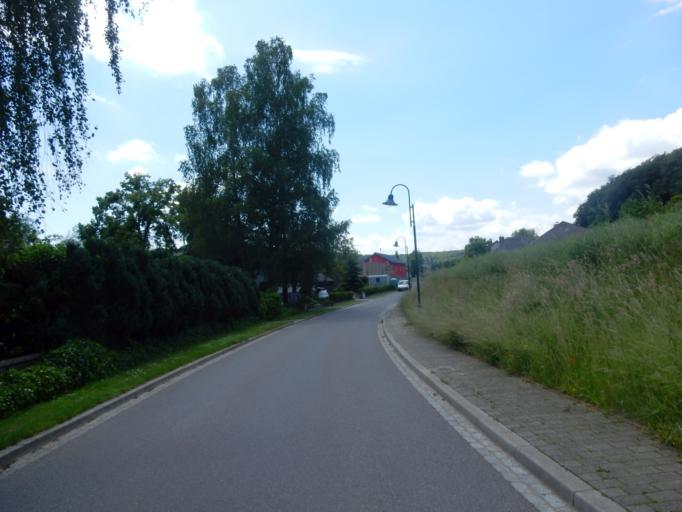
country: LU
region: Luxembourg
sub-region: Canton de Mersch
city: Tuntange
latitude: 49.7400
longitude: 6.0315
